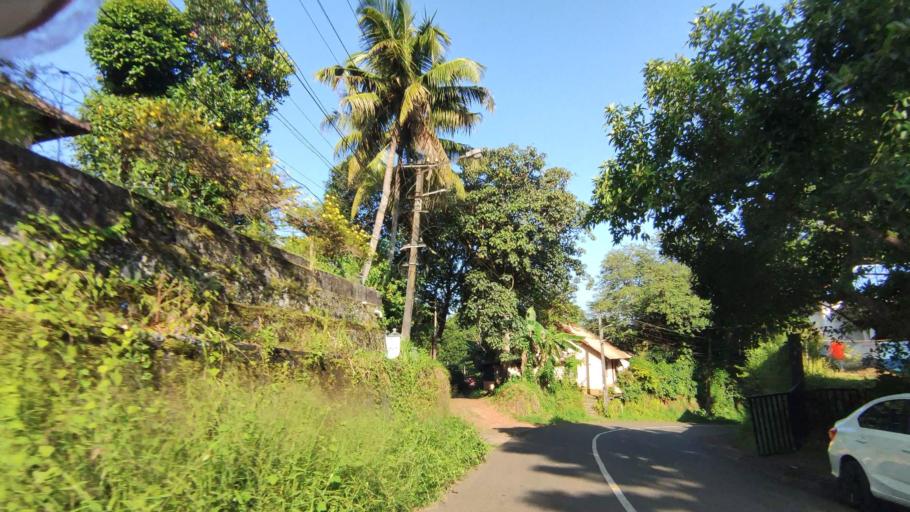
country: IN
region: Kerala
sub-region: Kottayam
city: Kottayam
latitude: 9.5586
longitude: 76.5139
